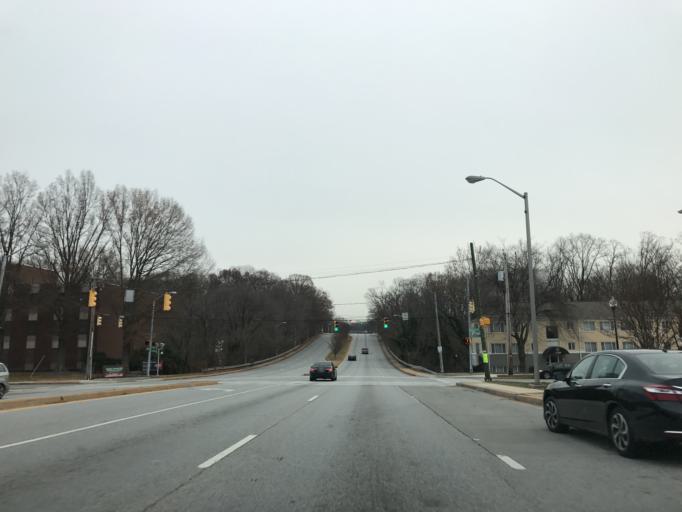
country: US
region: Maryland
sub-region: Baltimore County
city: Towson
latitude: 39.3669
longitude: -76.5817
